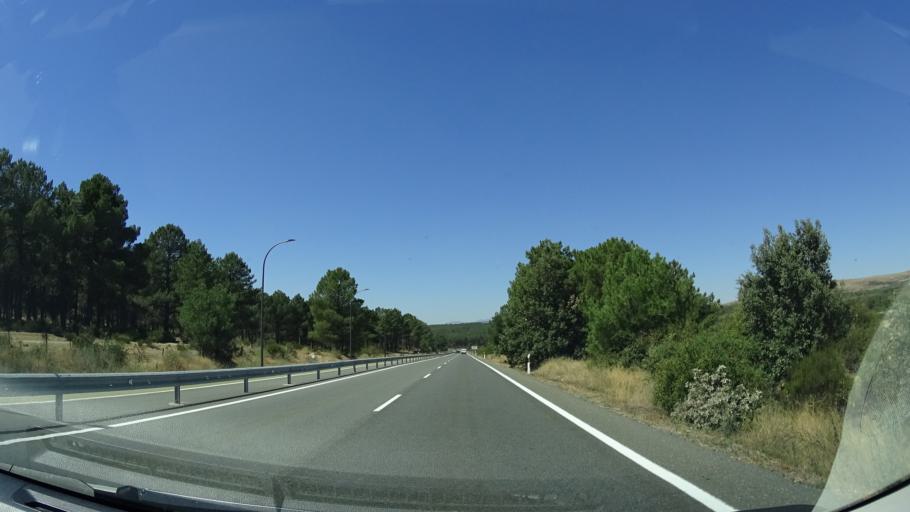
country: ES
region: Castille and Leon
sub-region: Provincia de Avila
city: Las Navas del Marques
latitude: 40.5962
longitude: -4.3508
